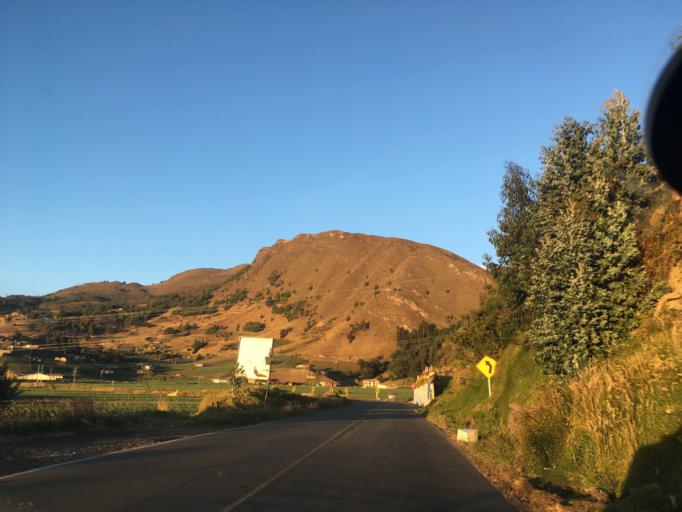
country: CO
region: Boyaca
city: Aquitania
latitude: 5.5540
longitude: -72.8801
